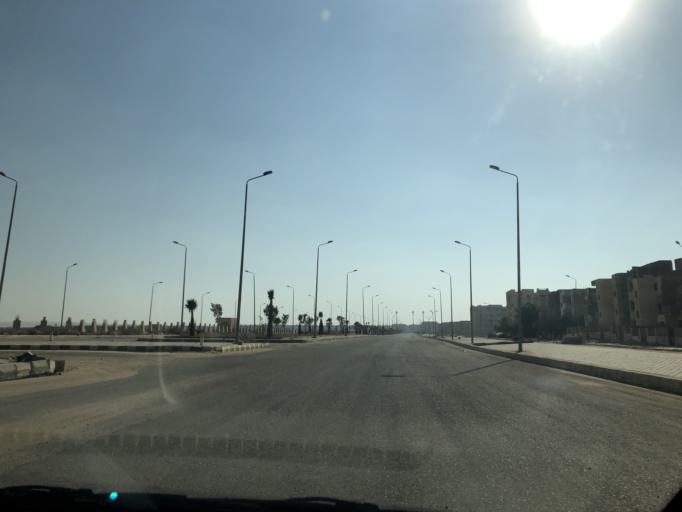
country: EG
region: Al Jizah
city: Madinat Sittah Uktubar
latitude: 29.9279
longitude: 31.0683
